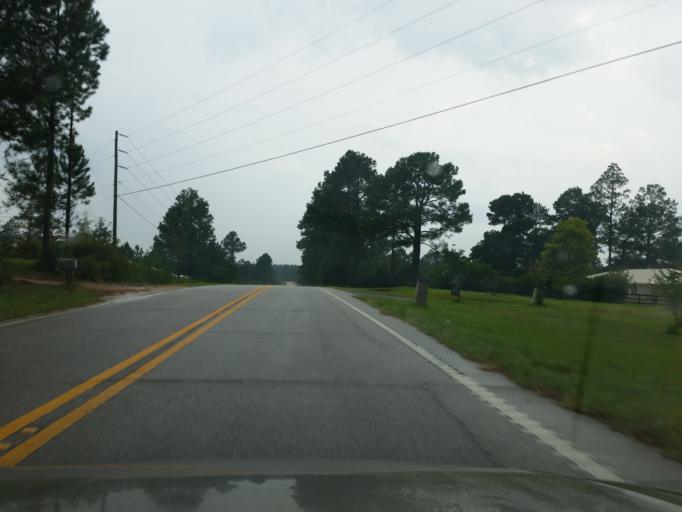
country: US
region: Alabama
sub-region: Baldwin County
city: Elberta
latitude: 30.5217
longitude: -87.4895
